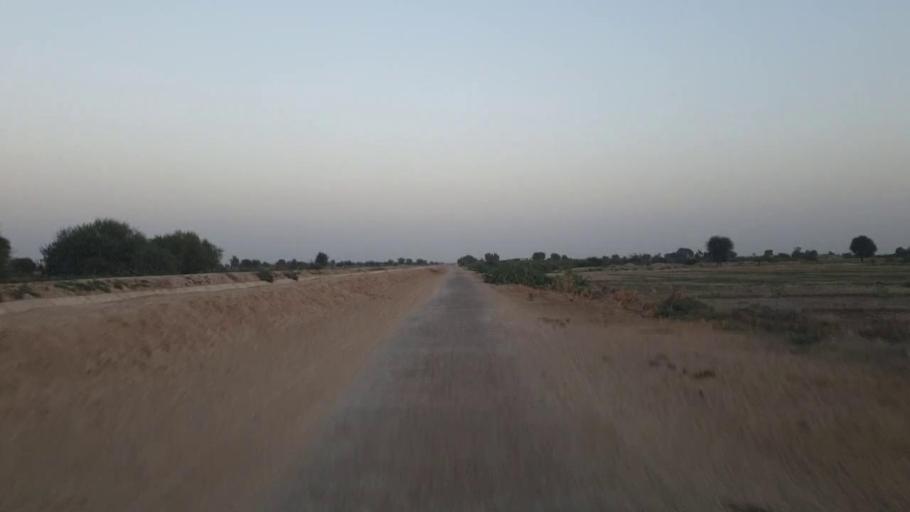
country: PK
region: Sindh
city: Umarkot
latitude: 25.4148
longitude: 69.6753
